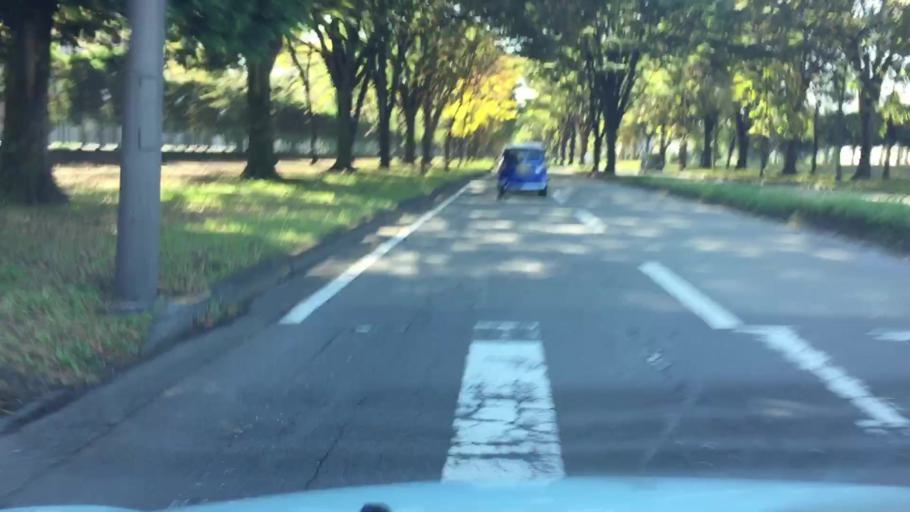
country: JP
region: Tochigi
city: Utsunomiya-shi
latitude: 36.5428
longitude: 139.9864
